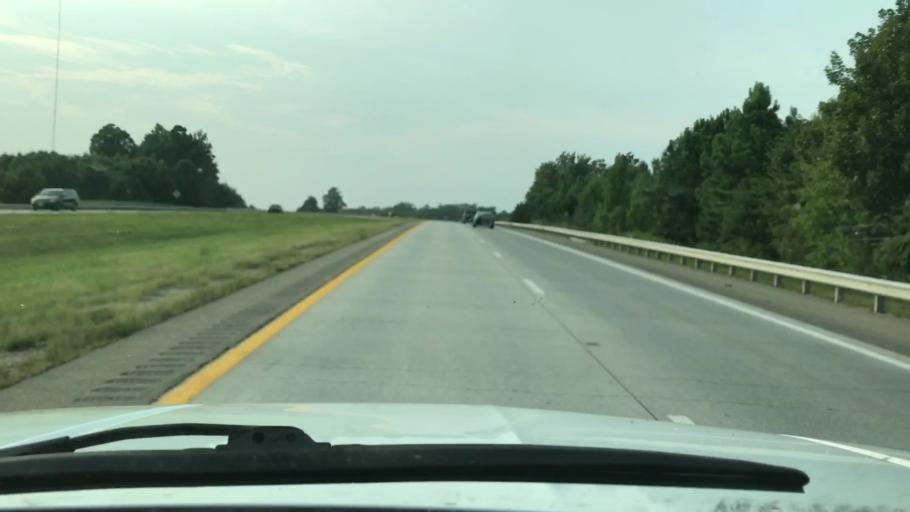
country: US
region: Virginia
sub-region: Chesterfield County
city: Brandermill
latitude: 37.4960
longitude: -77.6836
